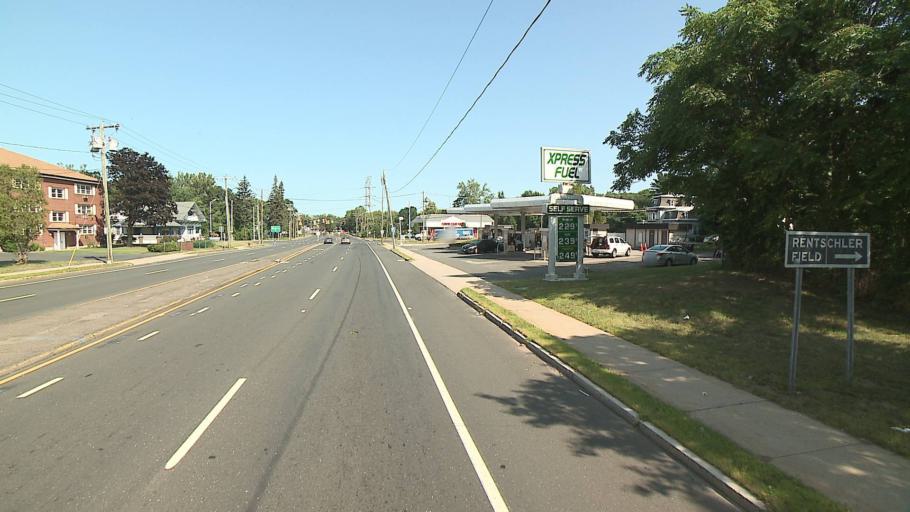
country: US
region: Connecticut
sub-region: Hartford County
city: East Hartford
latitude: 41.7594
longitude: -72.6441
